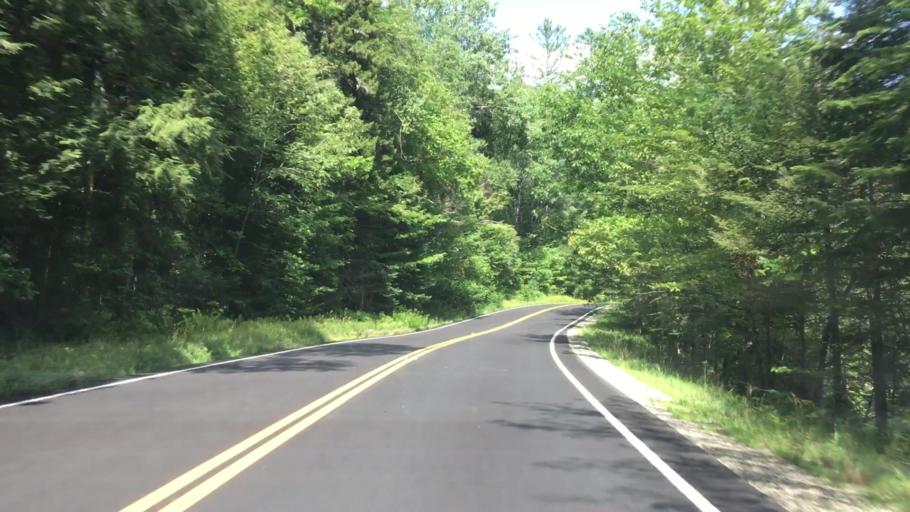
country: US
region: New Hampshire
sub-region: Grafton County
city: North Haverhill
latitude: 44.1017
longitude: -71.8579
